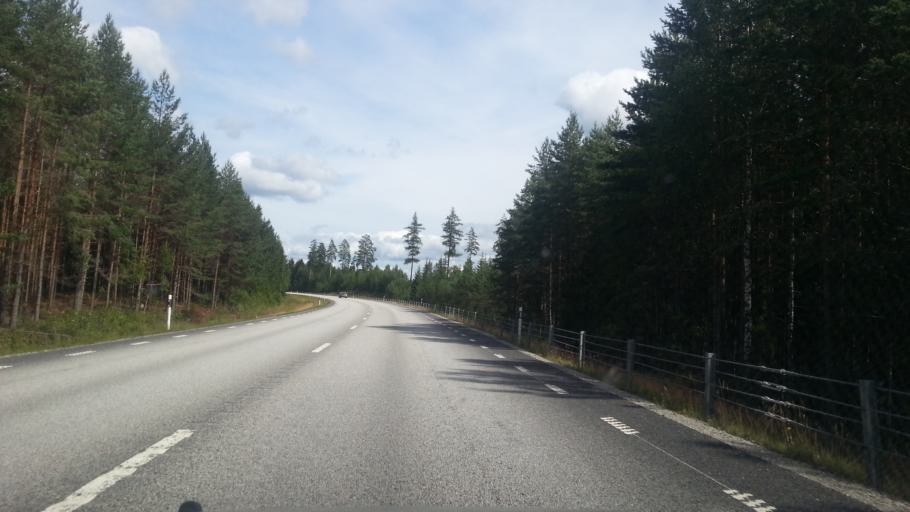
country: SE
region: OErebro
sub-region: Lindesbergs Kommun
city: Lindesberg
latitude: 59.6948
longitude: 15.3719
